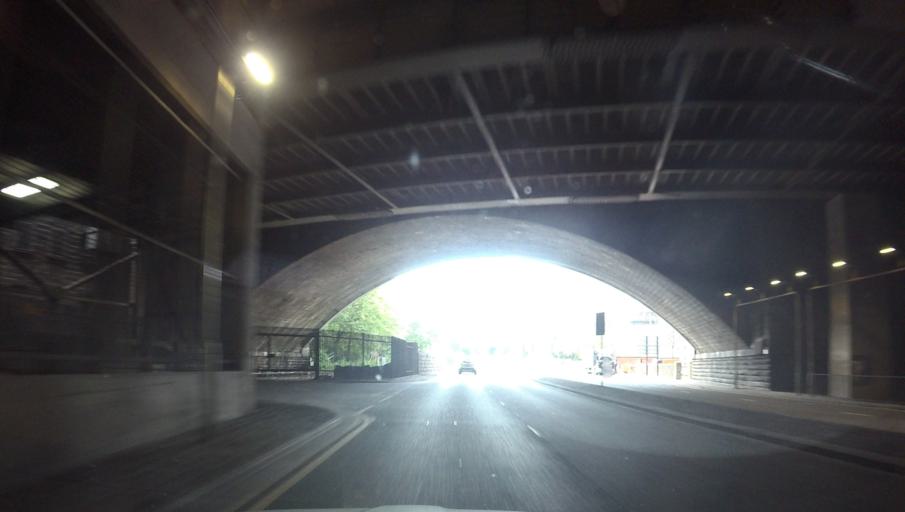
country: GB
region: Scotland
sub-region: Aberdeen City
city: Aberdeen
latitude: 57.1452
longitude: -2.0995
